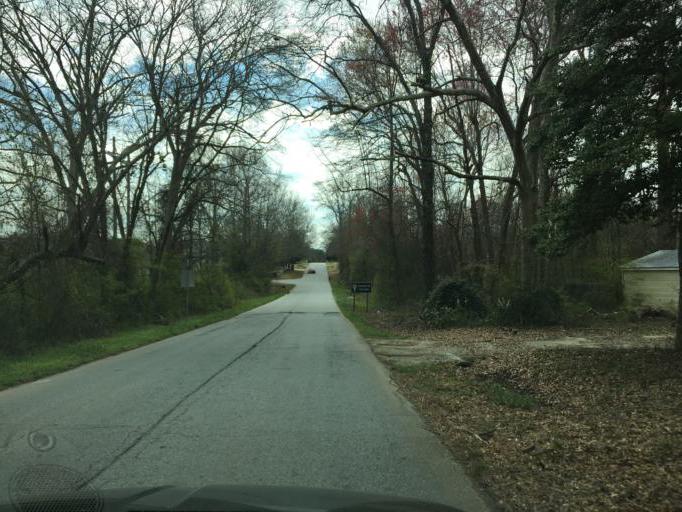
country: US
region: South Carolina
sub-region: Greenville County
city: Fountain Inn
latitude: 34.6987
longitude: -82.2245
